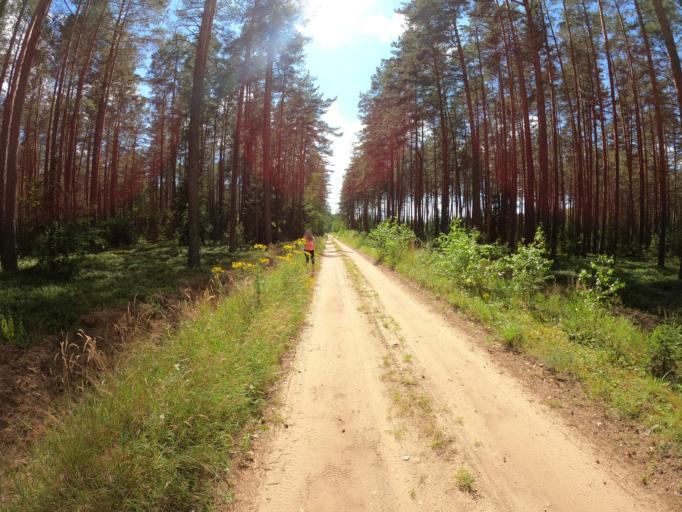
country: LT
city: Veisiejai
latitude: 54.0143
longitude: 23.8142
